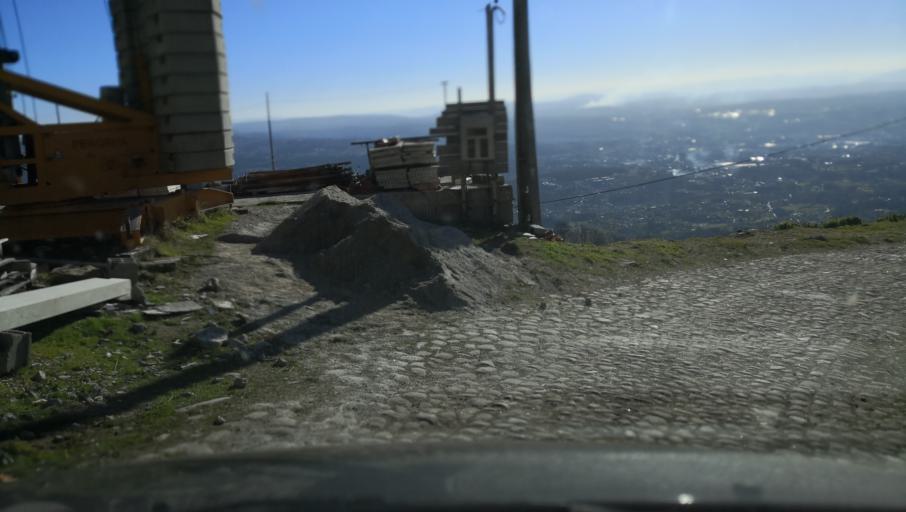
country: PT
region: Vila Real
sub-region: Vila Real
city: Vila Real
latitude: 41.3492
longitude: -7.7625
